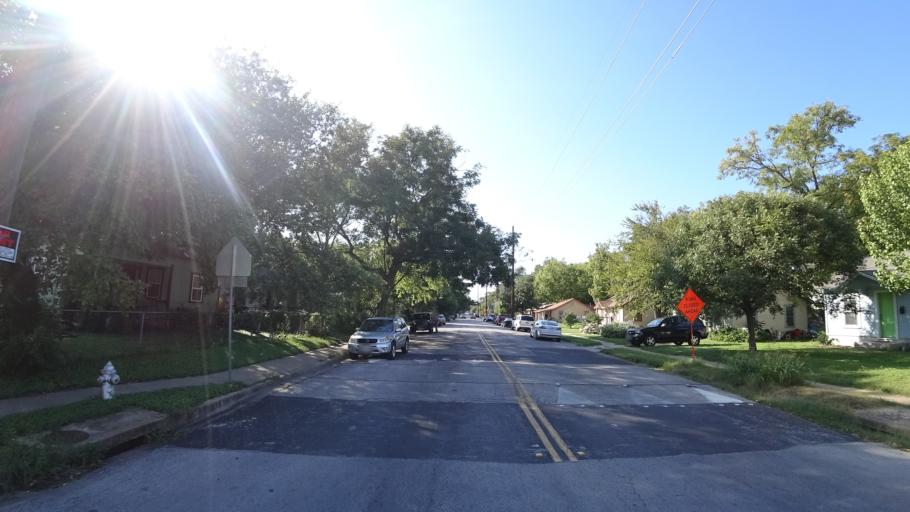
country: US
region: Texas
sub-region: Travis County
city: Austin
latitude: 30.2526
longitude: -97.7238
